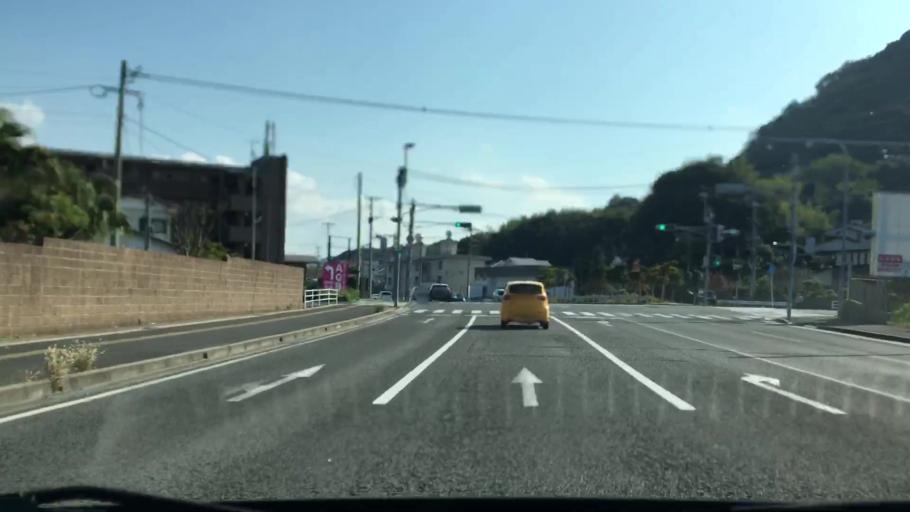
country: JP
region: Nagasaki
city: Togitsu
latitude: 32.8472
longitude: 129.8307
